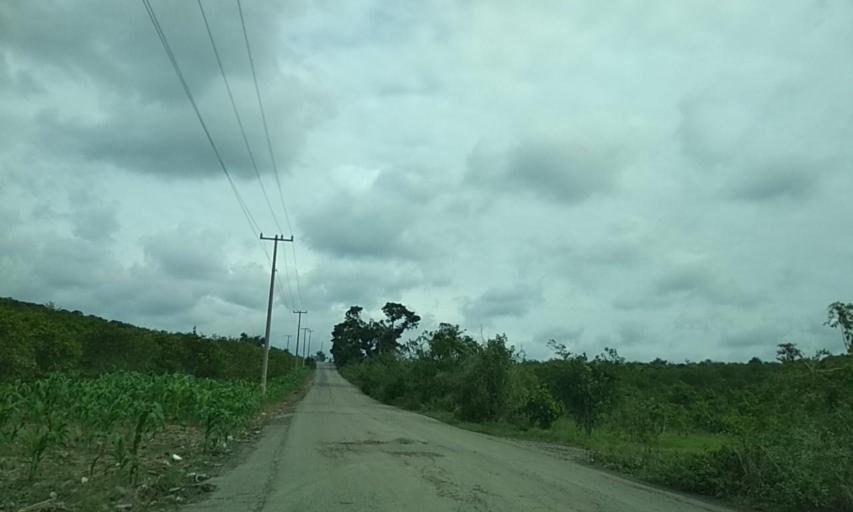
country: MX
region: Veracruz
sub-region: Papantla
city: El Chote
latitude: 20.3552
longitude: -97.3472
